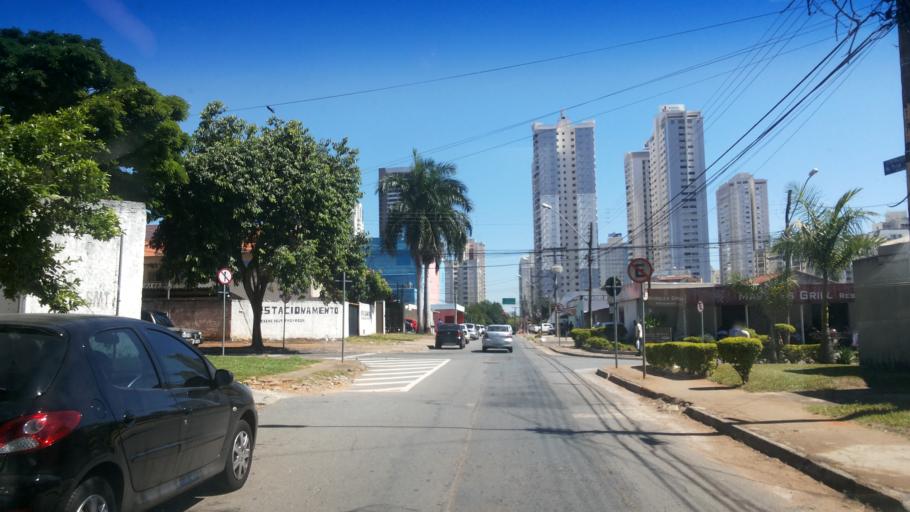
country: BR
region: Goias
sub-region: Goiania
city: Goiania
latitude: -16.7202
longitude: -49.2615
